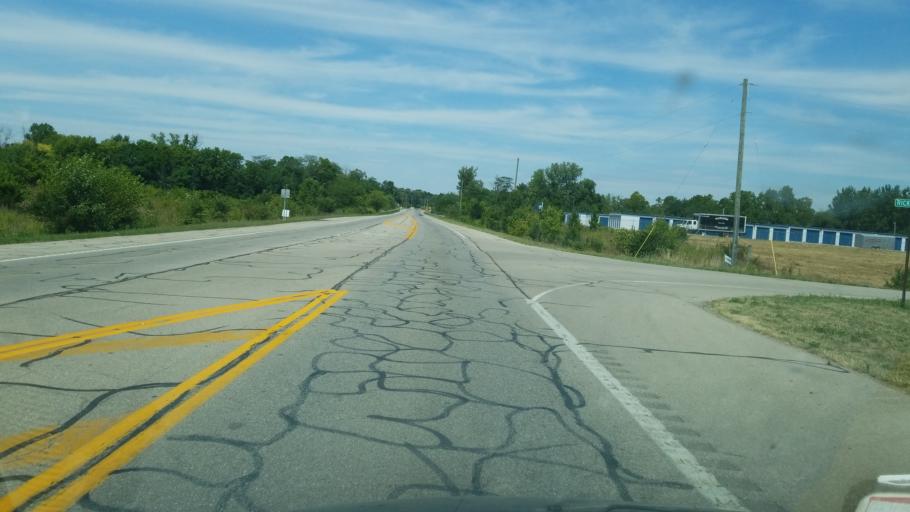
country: US
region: Ohio
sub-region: Madison County
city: Plain City
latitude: 40.1203
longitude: -83.2723
